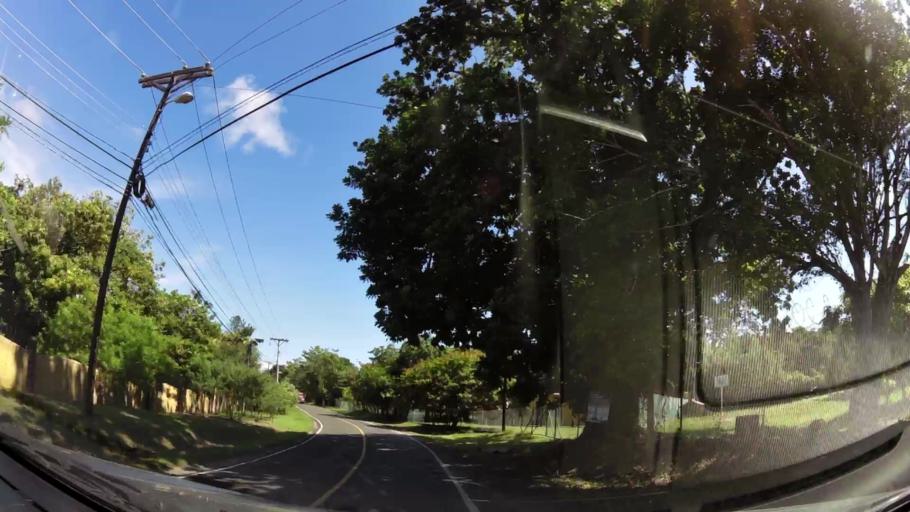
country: PA
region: Panama
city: Nueva Gorgona
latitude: 8.5589
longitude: -79.8868
